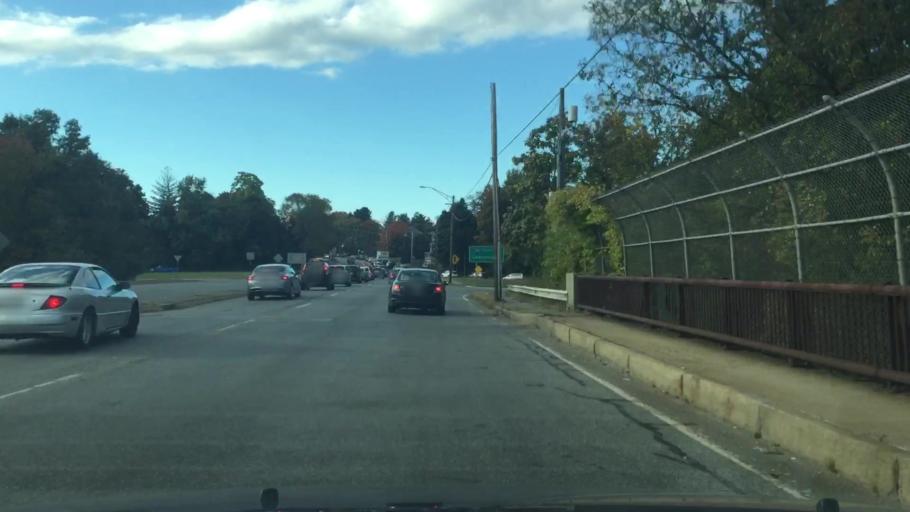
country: US
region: Massachusetts
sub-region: Essex County
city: Haverhill
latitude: 42.7994
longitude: -71.0916
